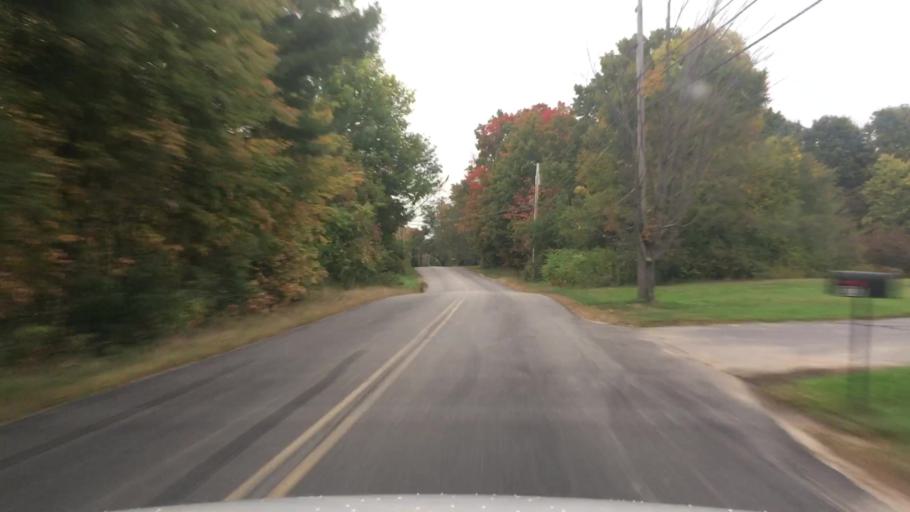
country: US
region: Maine
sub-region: York County
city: Buxton
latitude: 43.6256
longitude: -70.5355
